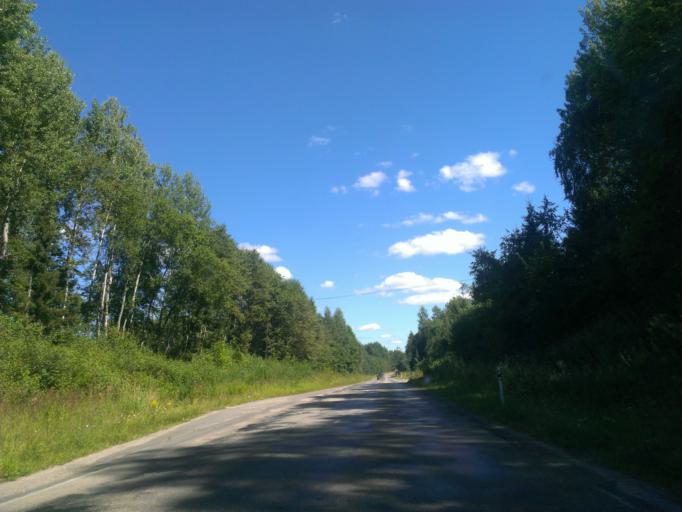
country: LV
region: Malpils
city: Malpils
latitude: 57.0175
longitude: 24.8995
